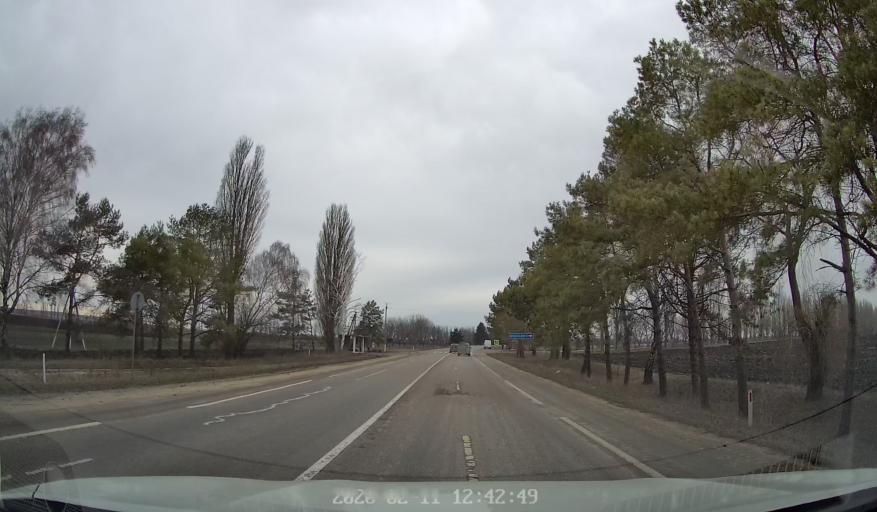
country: MD
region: Raionul Edinet
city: Edinet
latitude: 48.2264
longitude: 27.2169
